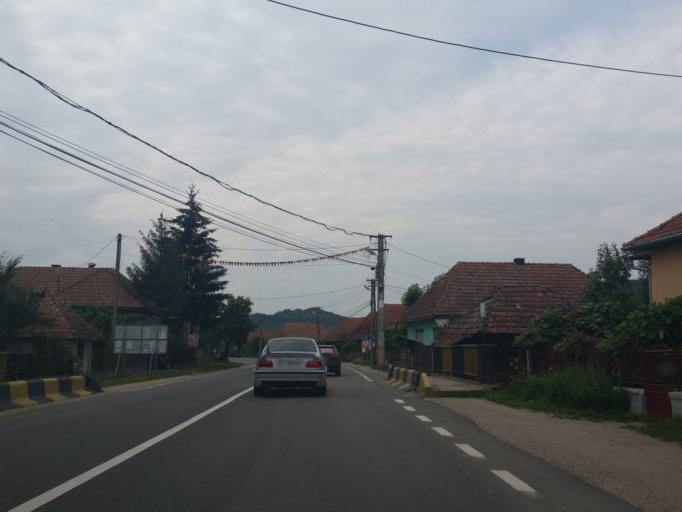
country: RO
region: Salaj
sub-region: Comuna Hida
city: Hida
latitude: 47.0376
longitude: 23.2661
